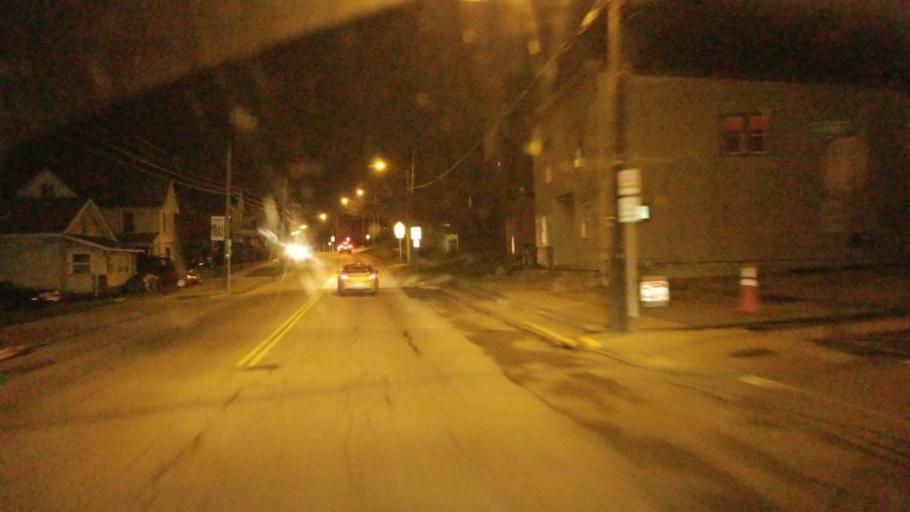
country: US
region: Ohio
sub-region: Wayne County
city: Apple Creek
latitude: 40.7494
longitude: -81.8360
